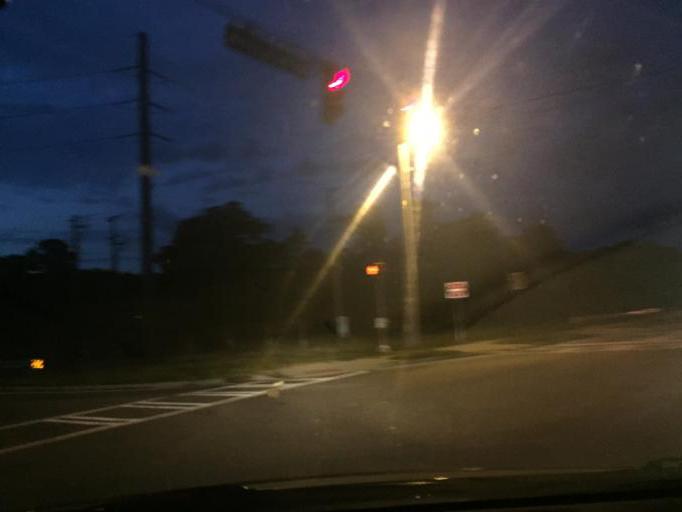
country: US
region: Georgia
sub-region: Chatham County
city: Montgomery
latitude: 31.9761
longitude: -81.1319
